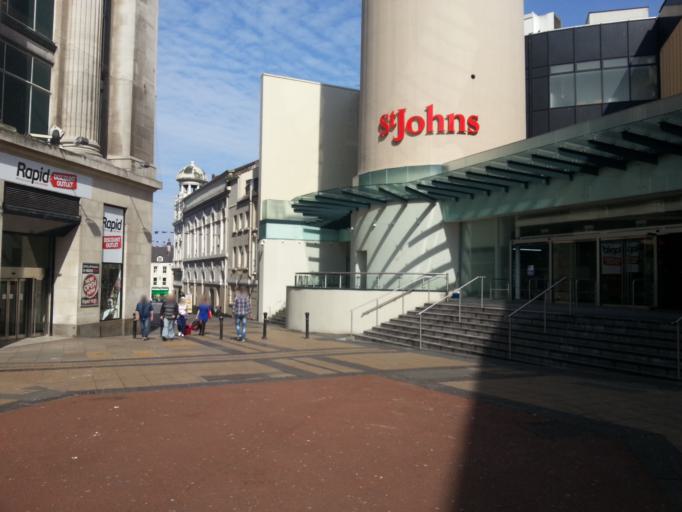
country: GB
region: England
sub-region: Liverpool
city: Liverpool
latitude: 53.4062
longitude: -2.9819
